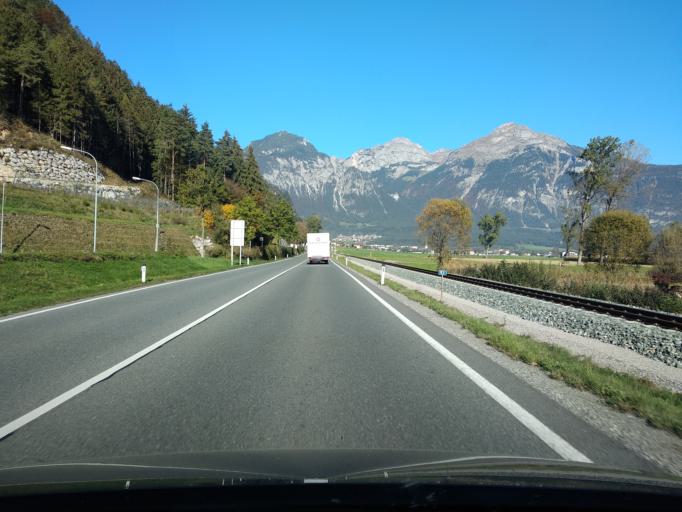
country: AT
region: Tyrol
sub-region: Politischer Bezirk Schwaz
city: Schlitters
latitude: 47.3831
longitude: 11.8322
